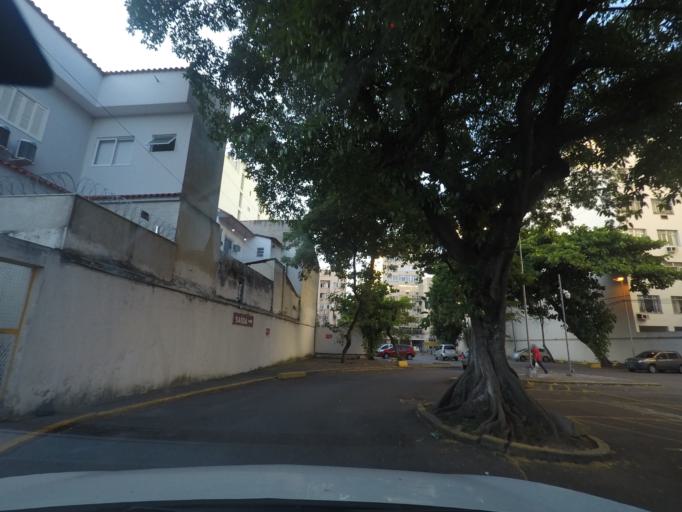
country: BR
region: Rio de Janeiro
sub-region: Rio De Janeiro
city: Rio de Janeiro
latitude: -22.9181
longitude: -43.2229
